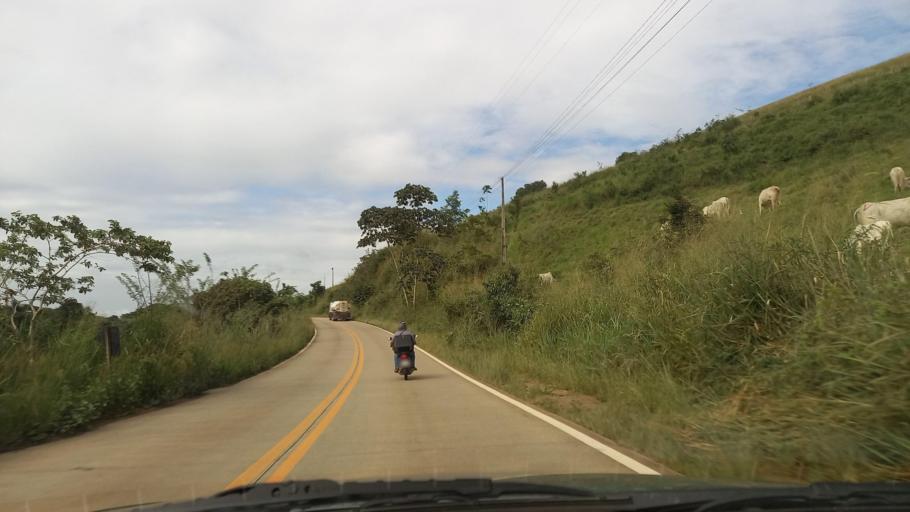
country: BR
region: Pernambuco
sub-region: Maraial
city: Maraial
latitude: -8.7502
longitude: -35.8202
